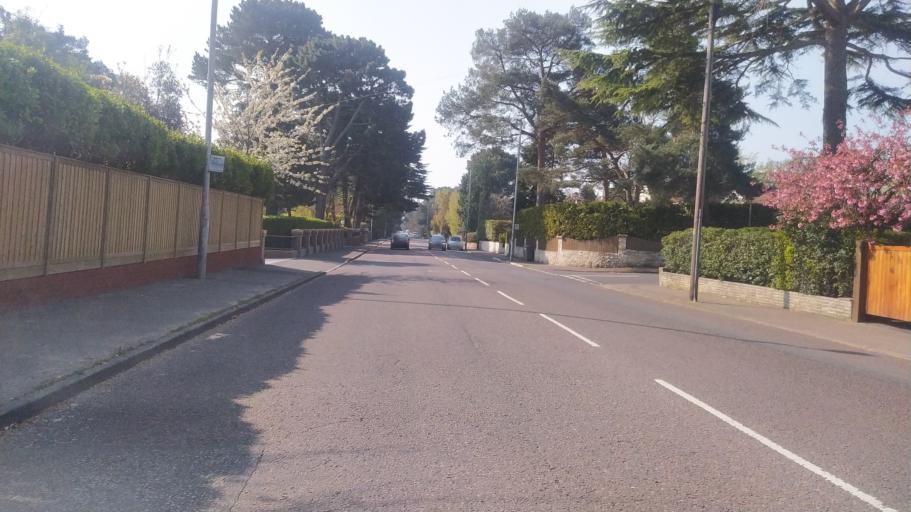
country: GB
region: England
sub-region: Dorset
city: Parkstone
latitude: 50.7165
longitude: -1.9256
